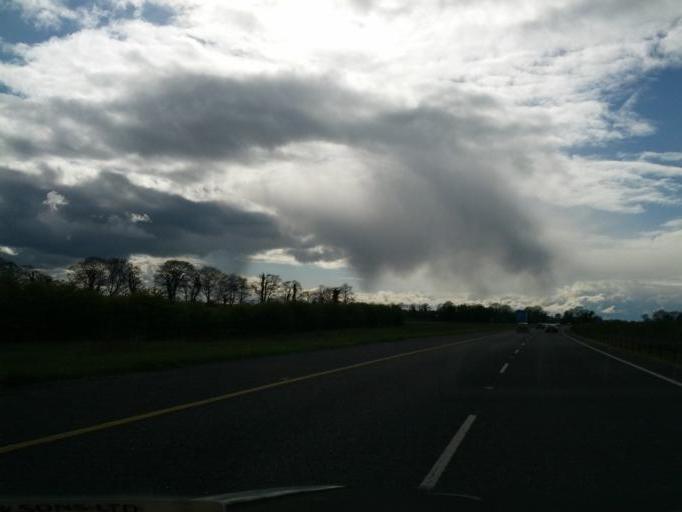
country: IE
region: Leinster
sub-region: An Mhi
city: Enfield
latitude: 53.4042
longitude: -6.8191
